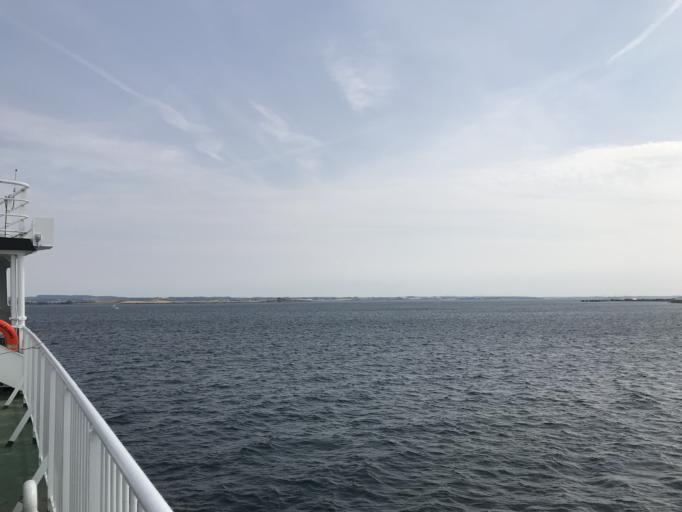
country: DK
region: South Denmark
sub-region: Faaborg-Midtfyn Kommune
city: Faaborg
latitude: 55.0379
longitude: 10.2281
